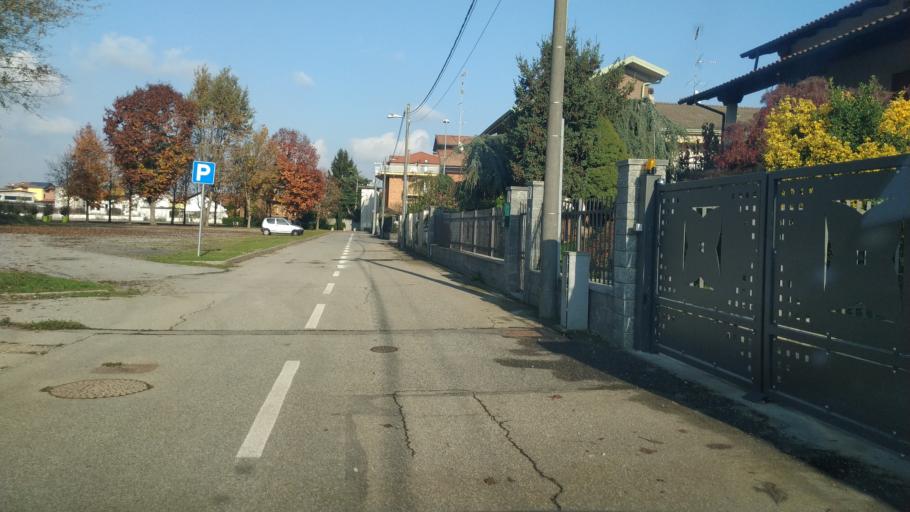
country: IT
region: Piedmont
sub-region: Provincia di Vercelli
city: Borgo Vercelli
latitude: 45.3542
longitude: 8.4597
